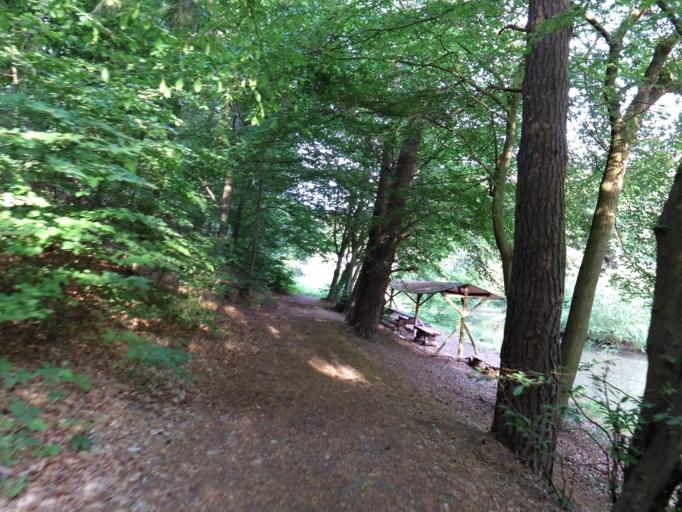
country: DE
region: Thuringia
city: Frauensee
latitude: 50.9023
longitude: 10.1099
